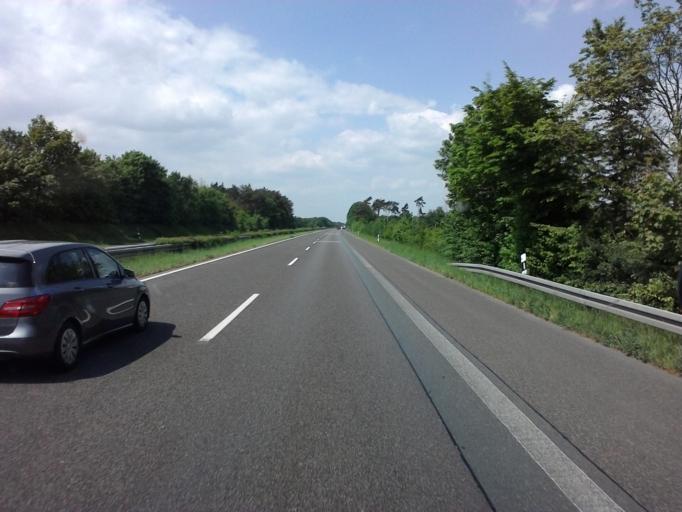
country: DE
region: North Rhine-Westphalia
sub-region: Regierungsbezirk Dusseldorf
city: Sonsbeck
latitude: 51.5807
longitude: 6.4048
